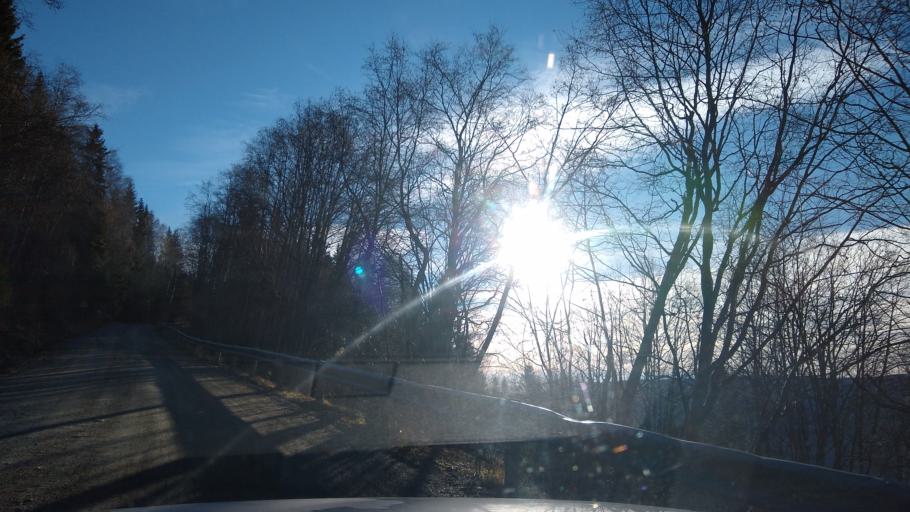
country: NO
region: Oppland
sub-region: Oyer
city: Tretten
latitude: 61.4096
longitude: 10.2501
